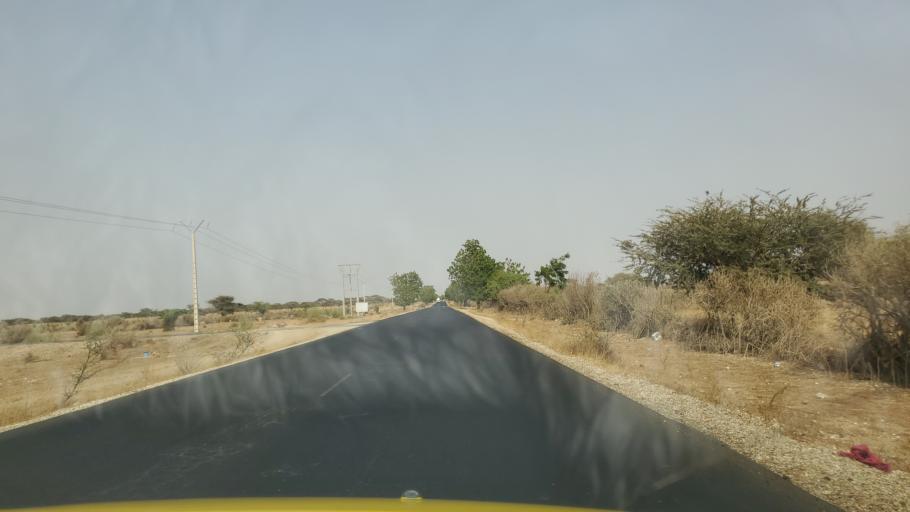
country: SN
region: Saint-Louis
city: Saint-Louis
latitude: 15.9245
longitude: -16.3101
